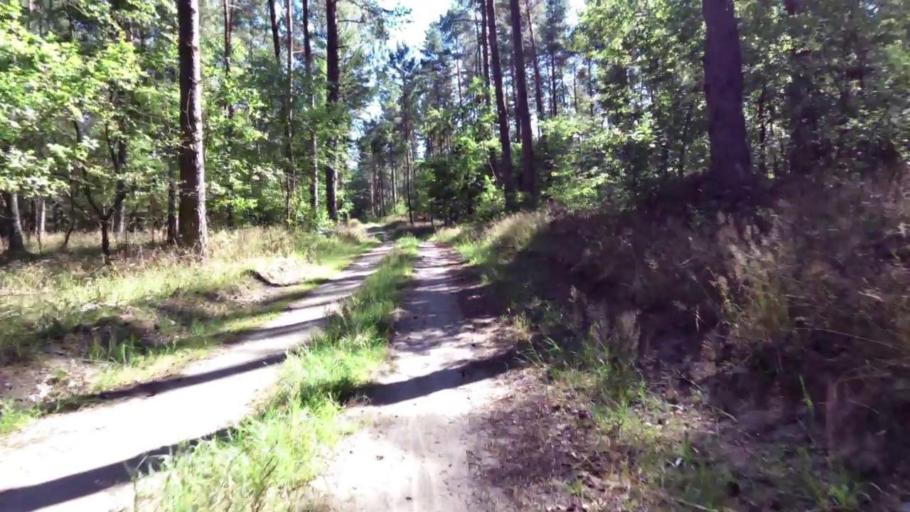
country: PL
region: West Pomeranian Voivodeship
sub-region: Powiat szczecinecki
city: Borne Sulinowo
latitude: 53.6023
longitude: 16.6072
